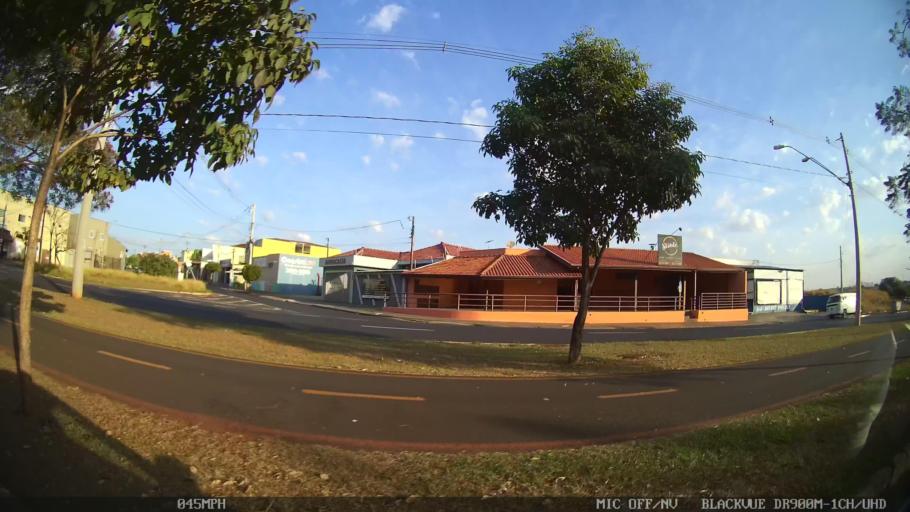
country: BR
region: Sao Paulo
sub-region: Ribeirao Preto
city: Ribeirao Preto
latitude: -21.1935
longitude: -47.7478
